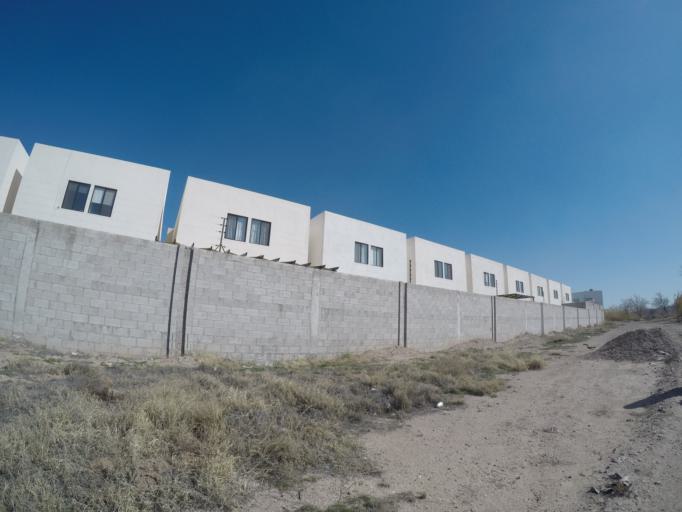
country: US
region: Texas
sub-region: El Paso County
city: Socorro
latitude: 31.6618
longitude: -106.3759
